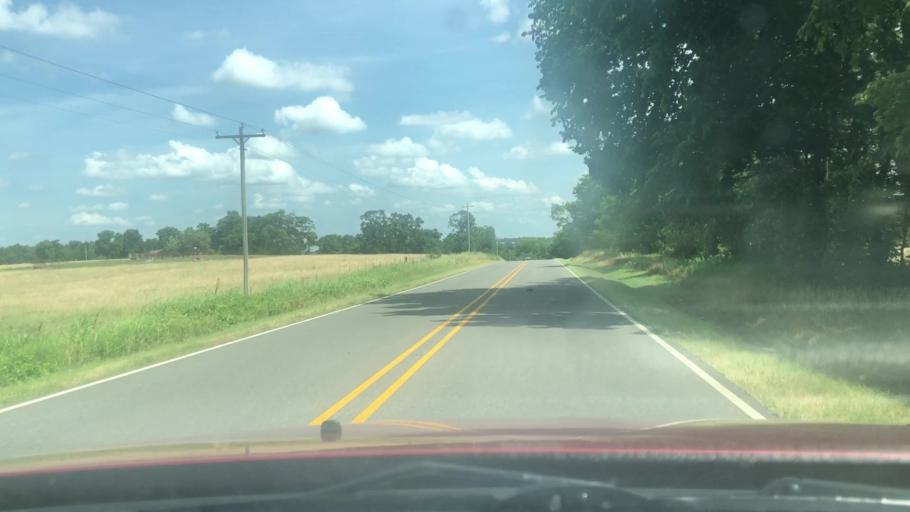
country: US
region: Arkansas
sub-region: Carroll County
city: Berryville
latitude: 36.3980
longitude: -93.5477
